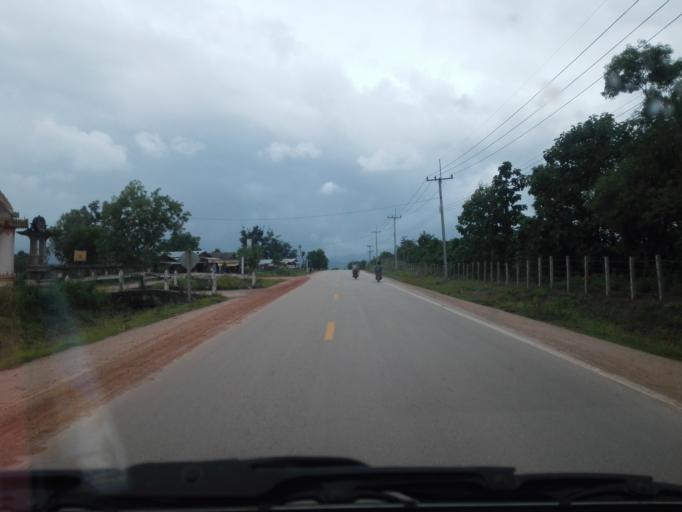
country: TH
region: Tak
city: Mae Sot
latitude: 16.6913
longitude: 98.4481
